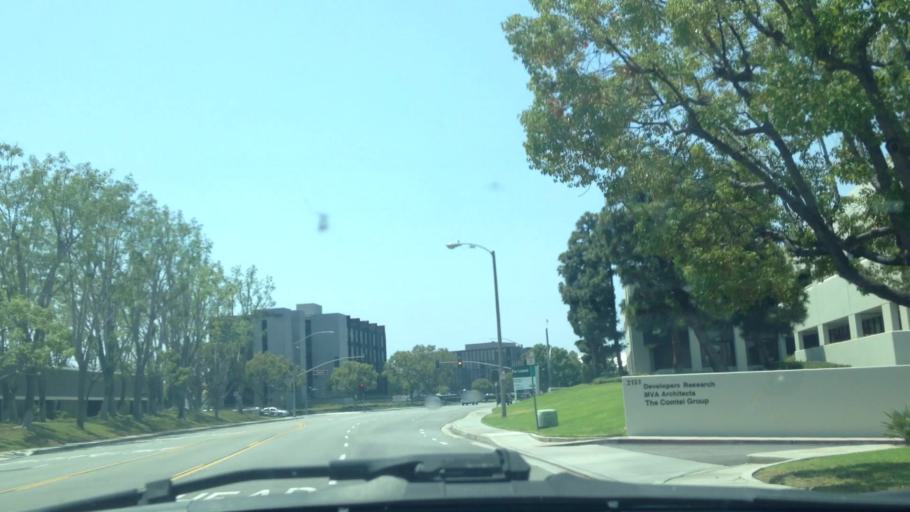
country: US
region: California
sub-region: Orange County
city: Irvine
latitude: 33.6770
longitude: -117.8566
